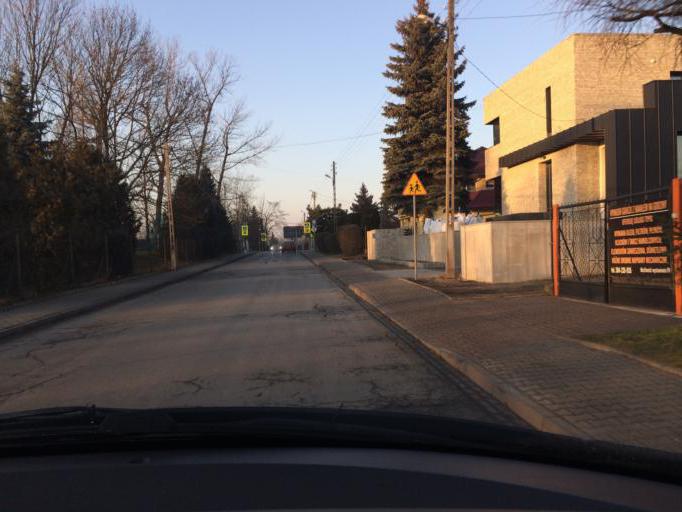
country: PL
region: Lesser Poland Voivodeship
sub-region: Powiat wielicki
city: Czarnochowice
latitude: 50.0142
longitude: 20.0423
